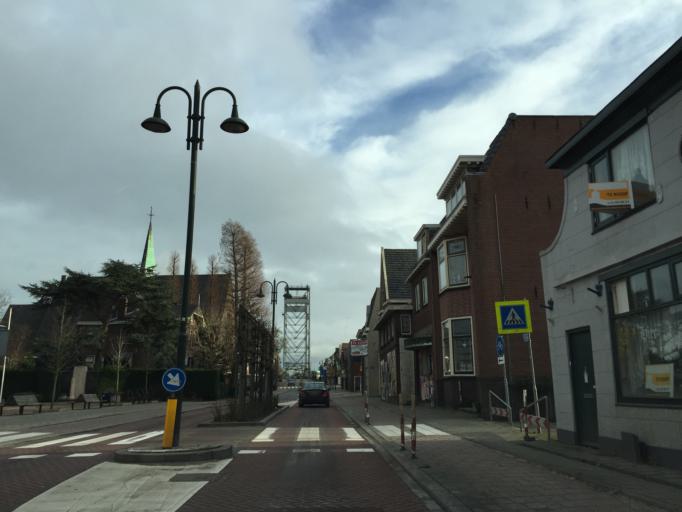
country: NL
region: South Holland
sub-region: Gemeente Boskoop
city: Boskoop
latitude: 52.0745
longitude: 4.6561
